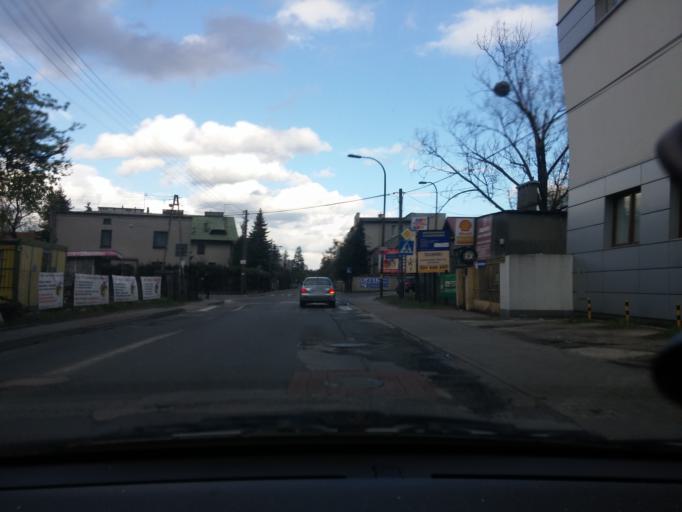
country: PL
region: Masovian Voivodeship
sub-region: Warszawa
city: Rembertow
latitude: 52.2273
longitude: 21.1475
